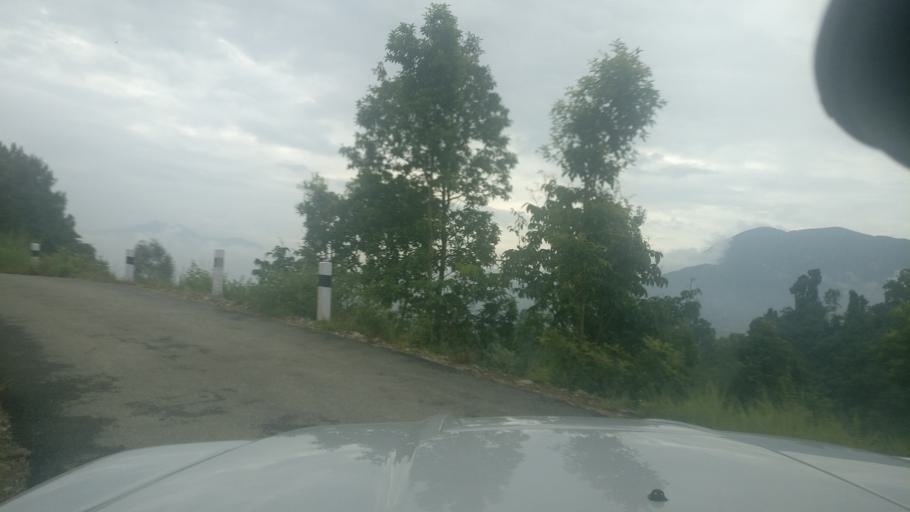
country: NP
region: Central Region
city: Kirtipur
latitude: 27.7043
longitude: 85.2543
